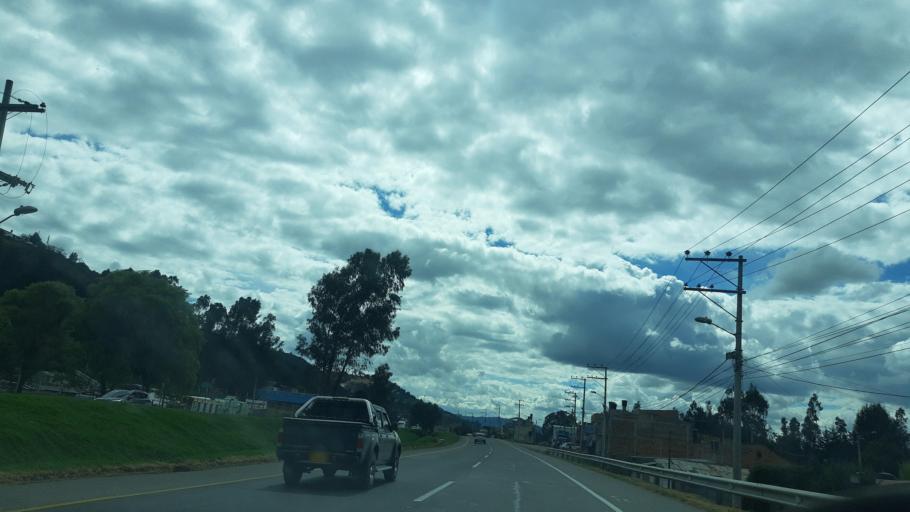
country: CO
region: Cundinamarca
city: Gachancipa
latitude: 4.9789
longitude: -73.8893
